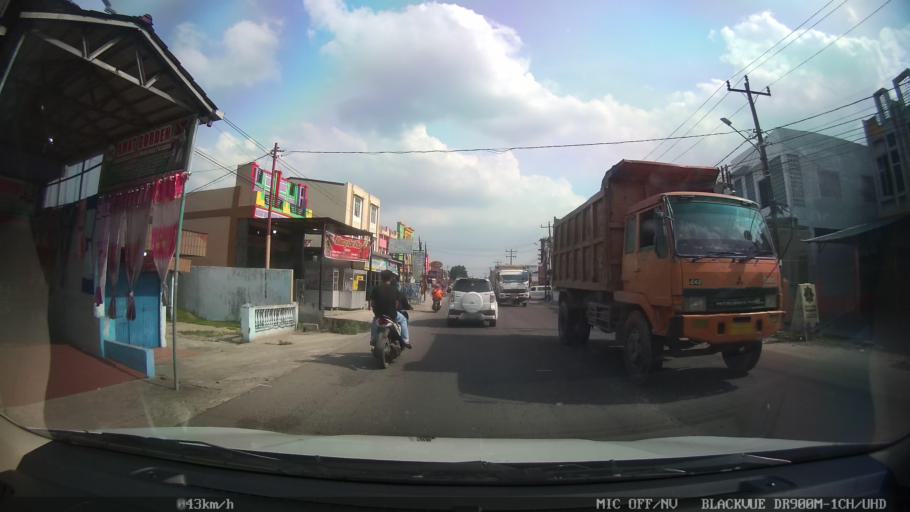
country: ID
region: North Sumatra
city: Binjai
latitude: 3.6213
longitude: 98.4961
